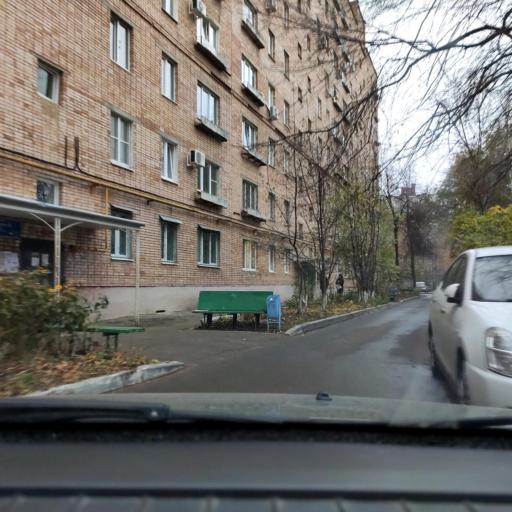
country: RU
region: Samara
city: Tol'yatti
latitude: 53.5053
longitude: 49.4246
